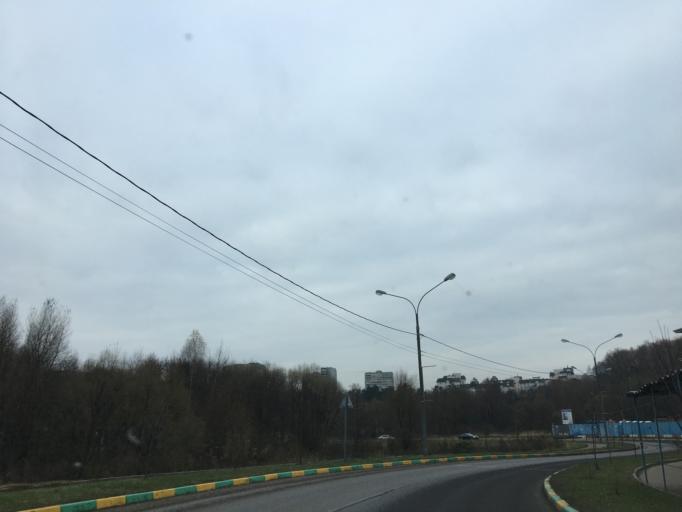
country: RU
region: Moskovskaya
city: Vidnoye
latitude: 55.5447
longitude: 37.6983
